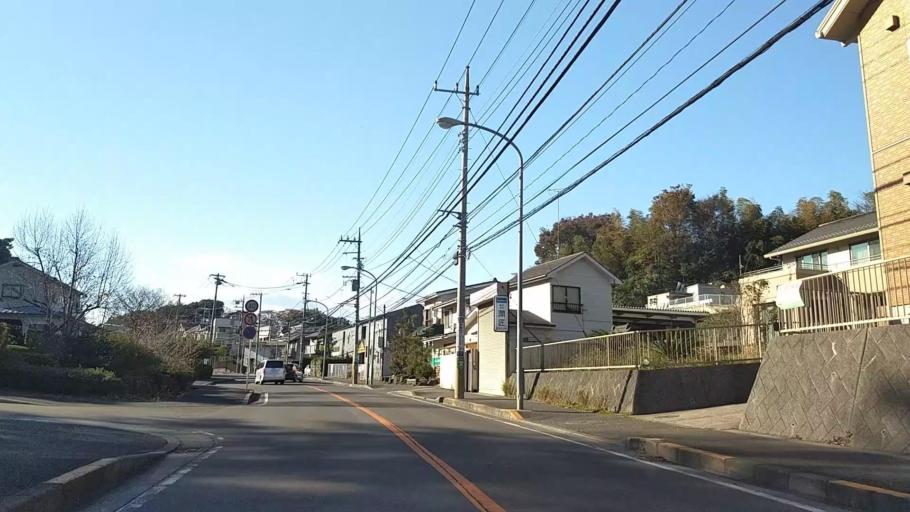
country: JP
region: Kanagawa
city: Yokohama
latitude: 35.5197
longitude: 139.5592
